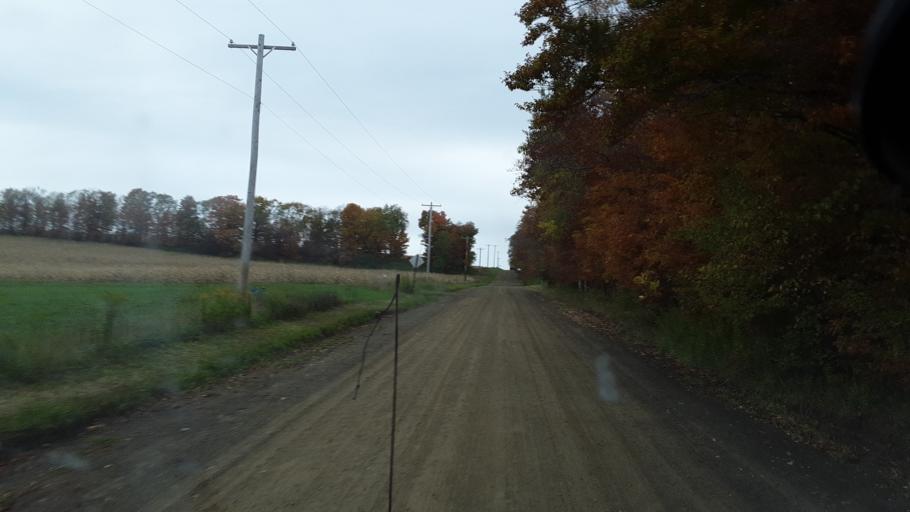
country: US
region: New York
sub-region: Allegany County
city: Andover
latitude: 42.0861
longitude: -77.7960
